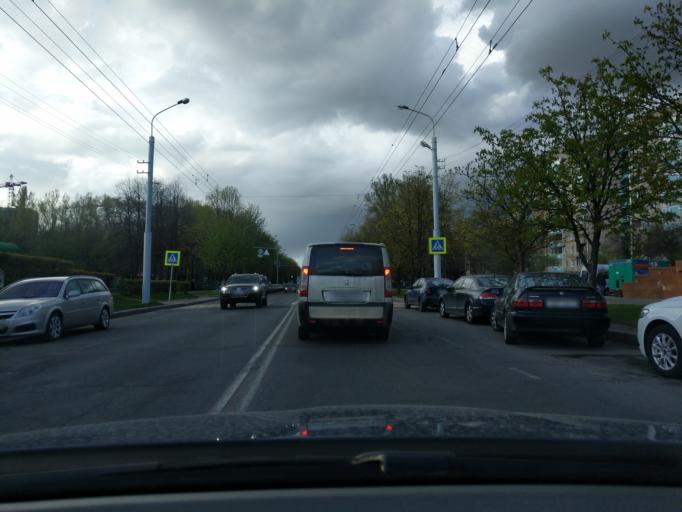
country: BY
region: Minsk
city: Novoye Medvezhino
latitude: 53.8956
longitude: 27.4813
